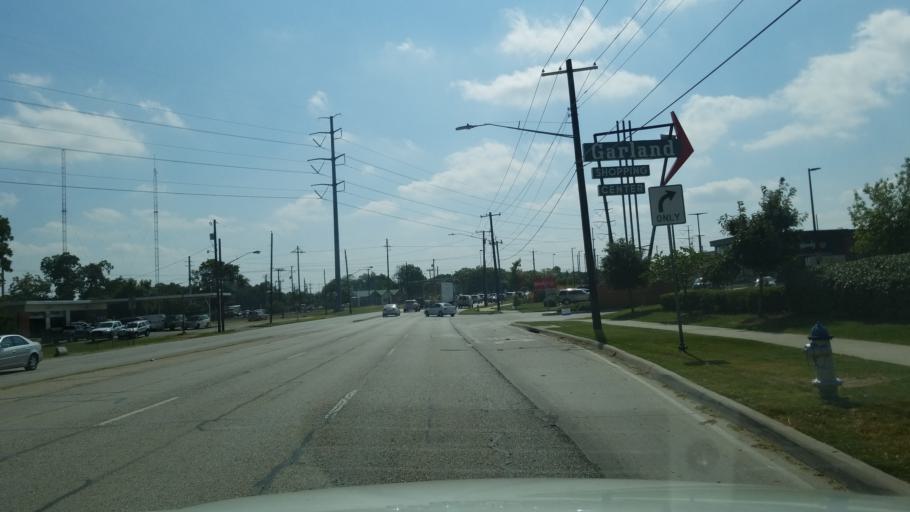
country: US
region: Texas
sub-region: Dallas County
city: Garland
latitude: 32.8962
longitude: -96.6489
